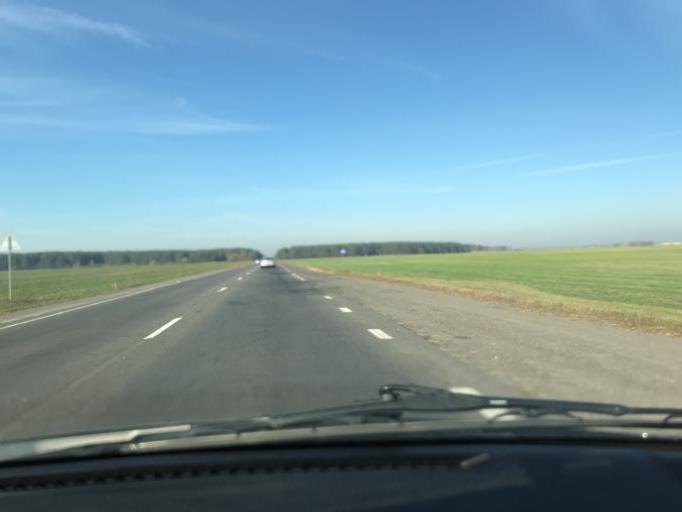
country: BY
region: Brest
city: Luninyets
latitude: 52.2540
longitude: 27.0535
